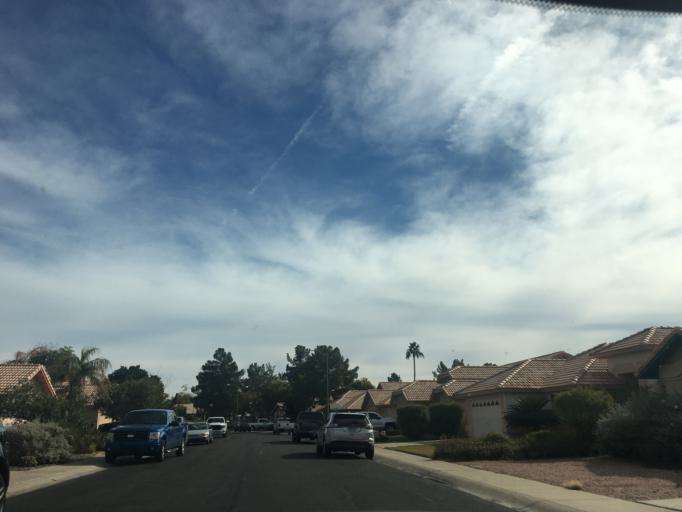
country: US
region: Arizona
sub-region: Maricopa County
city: Gilbert
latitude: 33.3462
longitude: -111.8046
